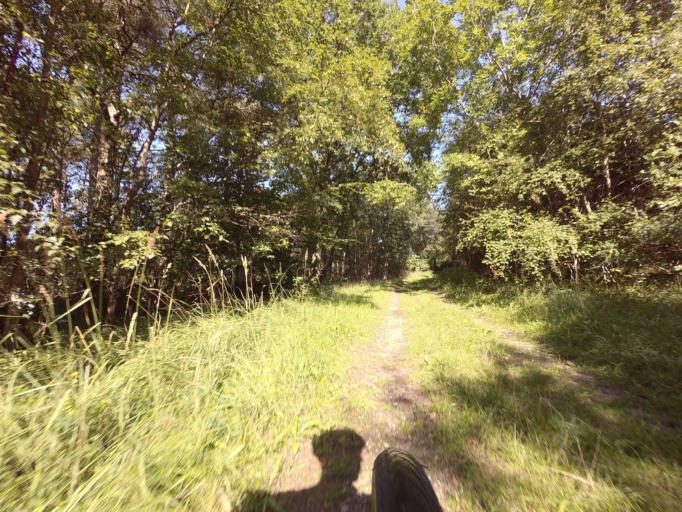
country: DK
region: North Denmark
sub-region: Hjorring Kommune
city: Hirtshals
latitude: 57.5843
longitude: 10.0027
